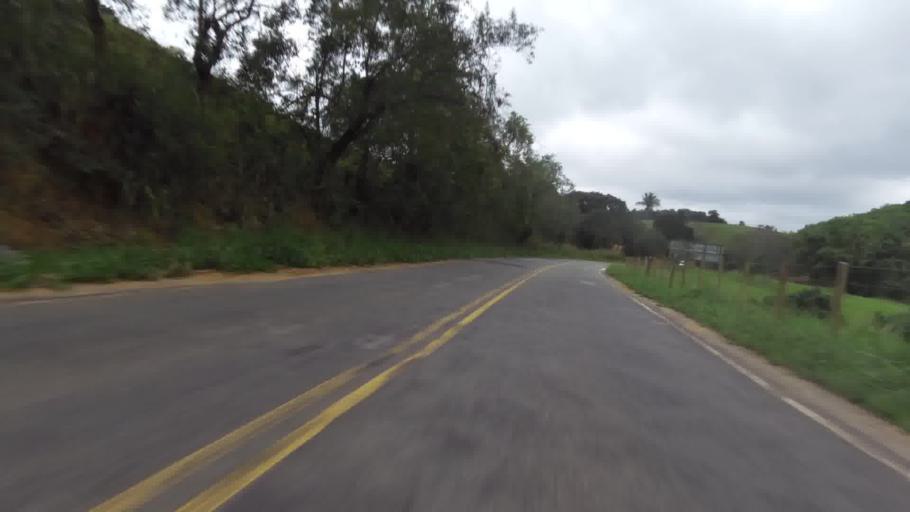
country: BR
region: Espirito Santo
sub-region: Alfredo Chaves
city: Alfredo Chaves
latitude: -20.6695
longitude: -40.7058
